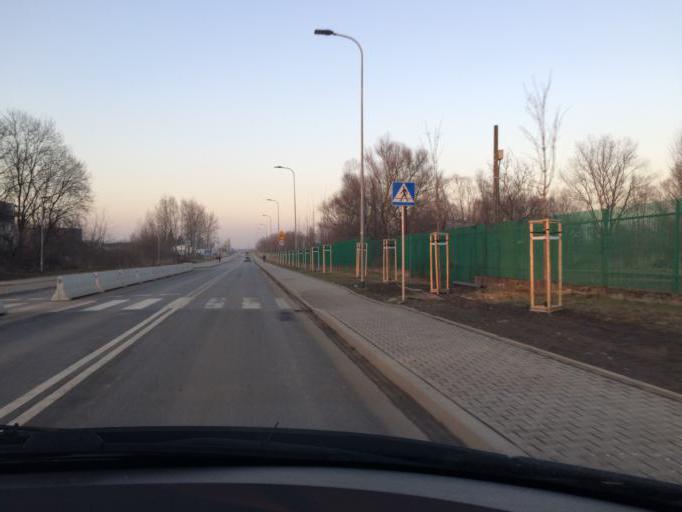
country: PL
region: Lesser Poland Voivodeship
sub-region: Powiat wielicki
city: Czarnochowice
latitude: 50.0248
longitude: 20.0513
